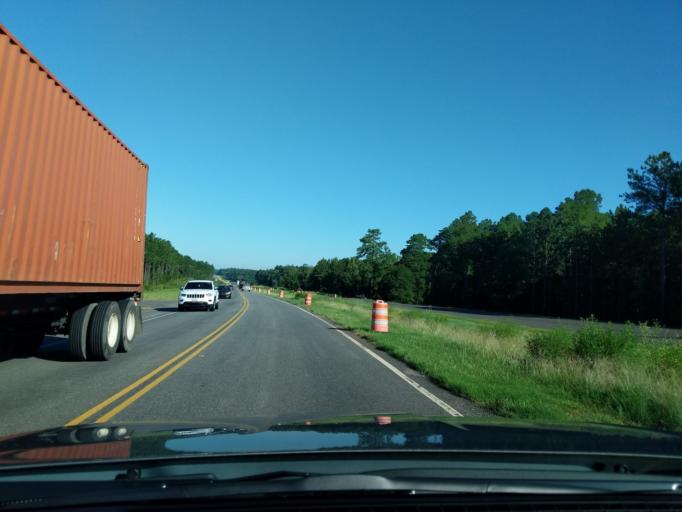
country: US
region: Georgia
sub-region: McDuffie County
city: Thomson
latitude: 33.5741
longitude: -82.5211
